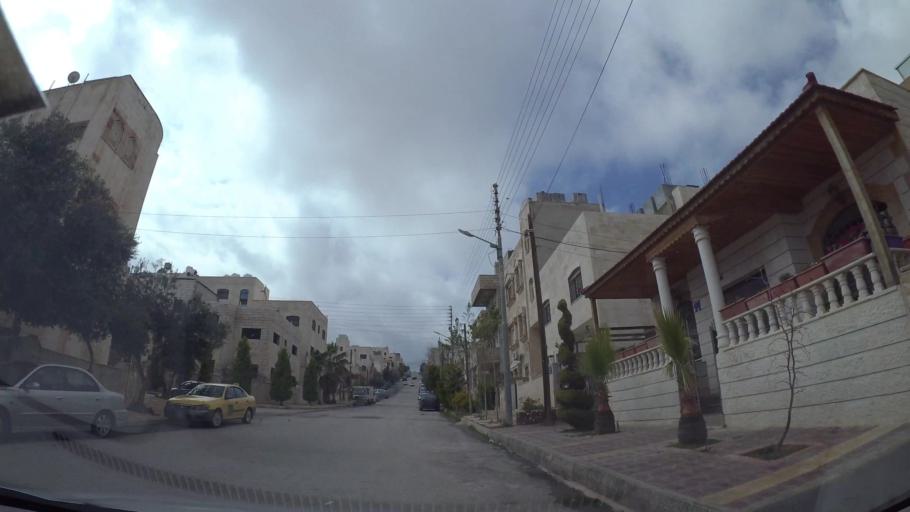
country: JO
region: Amman
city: Al Jubayhah
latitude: 32.0651
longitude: 35.8846
